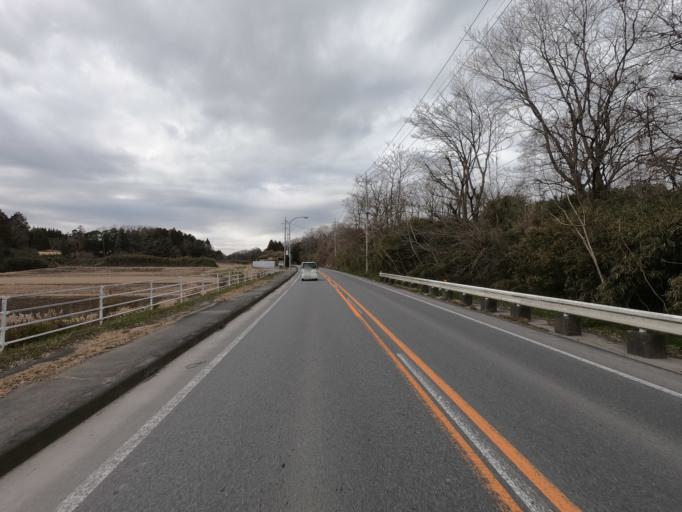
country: JP
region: Ibaraki
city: Ishioka
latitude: 36.0941
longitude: 140.3692
